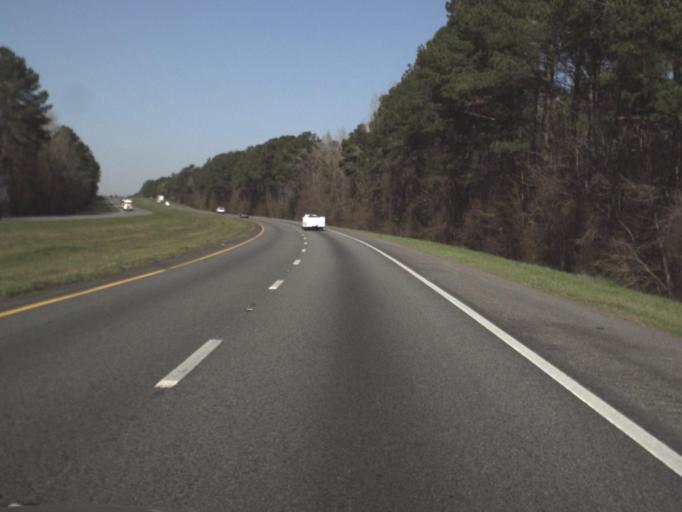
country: US
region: Florida
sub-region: Jefferson County
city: Monticello
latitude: 30.4868
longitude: -83.9531
